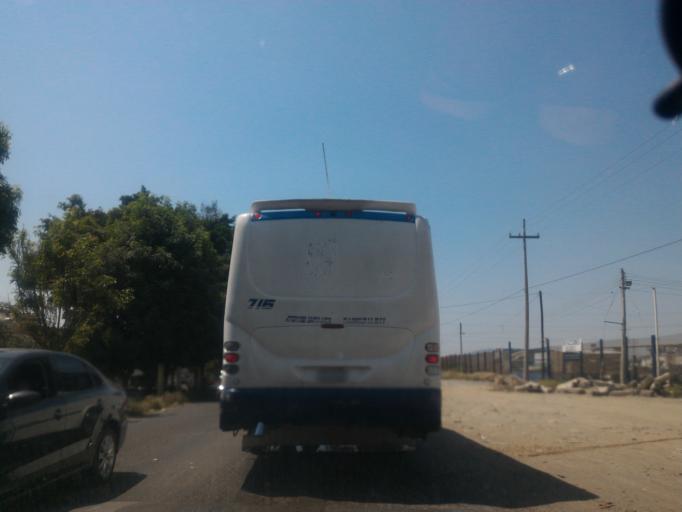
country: MX
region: Jalisco
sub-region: San Pedro Tlaquepaque
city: Paseo del Prado
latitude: 20.5654
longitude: -103.4116
